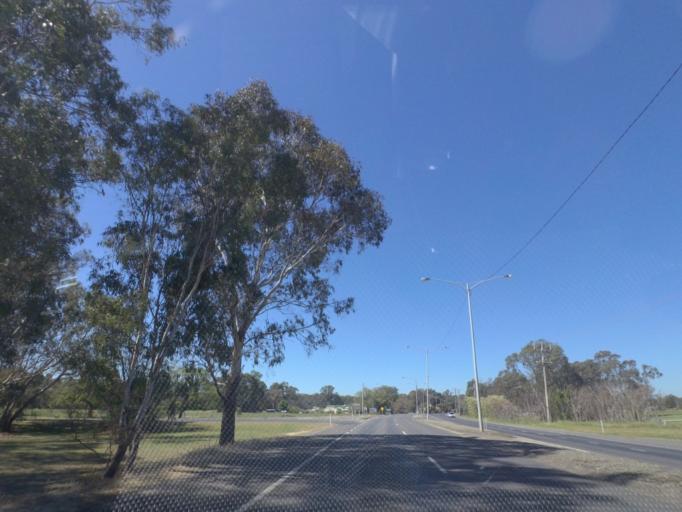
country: AU
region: Victoria
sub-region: Murrindindi
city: Kinglake West
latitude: -37.0227
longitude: 145.1154
